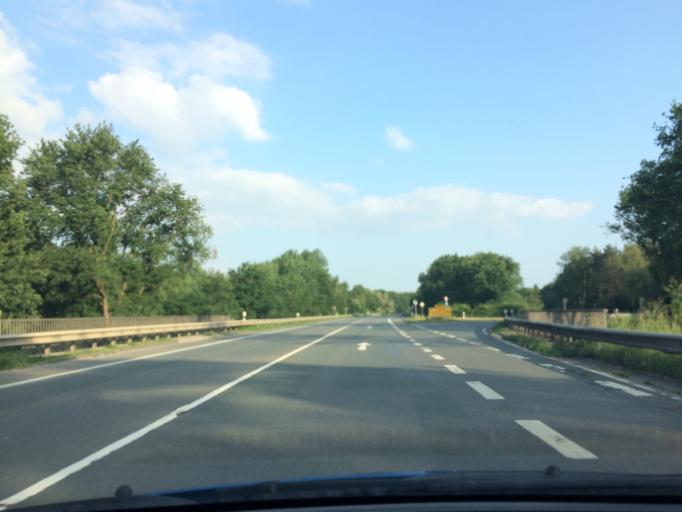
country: DE
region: North Rhine-Westphalia
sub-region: Regierungsbezirk Munster
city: Greven
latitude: 52.0604
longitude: 7.6747
